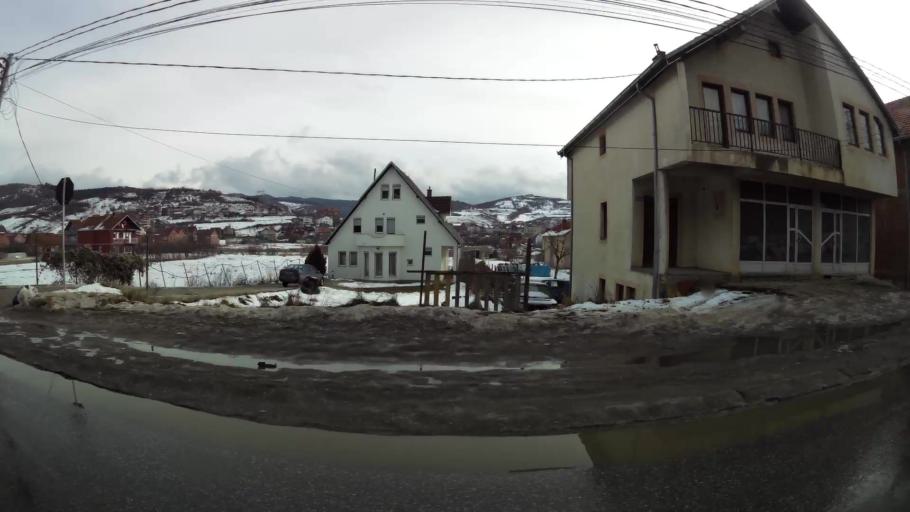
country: XK
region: Pristina
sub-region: Komuna e Prishtines
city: Pristina
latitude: 42.6867
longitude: 21.1767
